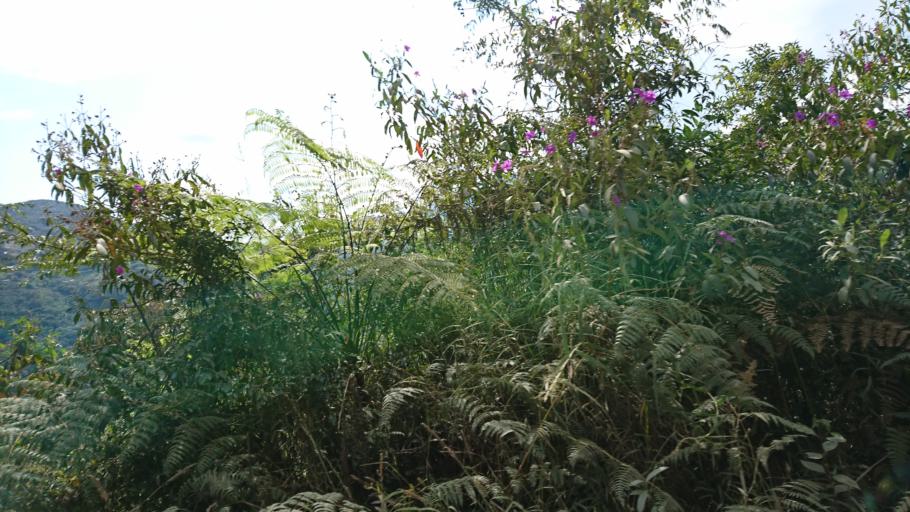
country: BO
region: La Paz
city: Coroico
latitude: -16.1095
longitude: -67.7782
